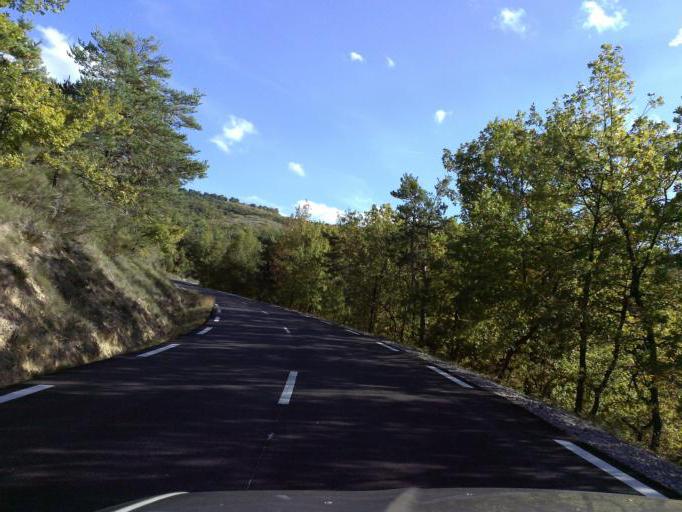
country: FR
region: Provence-Alpes-Cote d'Azur
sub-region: Departement des Alpes-de-Haute-Provence
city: Riez
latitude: 43.9067
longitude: 6.1402
